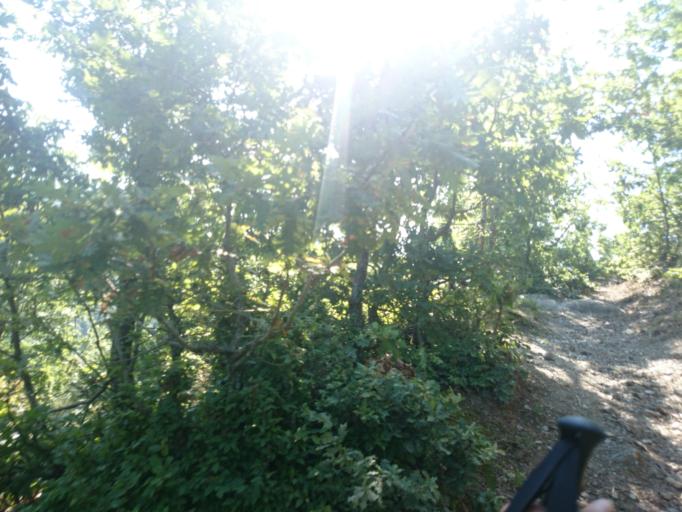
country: AL
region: Diber
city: Peshkopi
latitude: 41.6377
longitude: 20.4093
